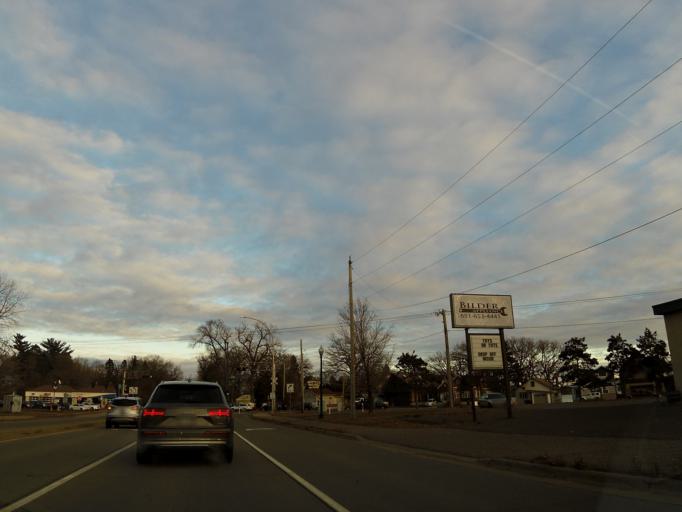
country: US
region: Minnesota
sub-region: Ramsey County
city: White Bear Lake
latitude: 45.0792
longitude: -93.0170
